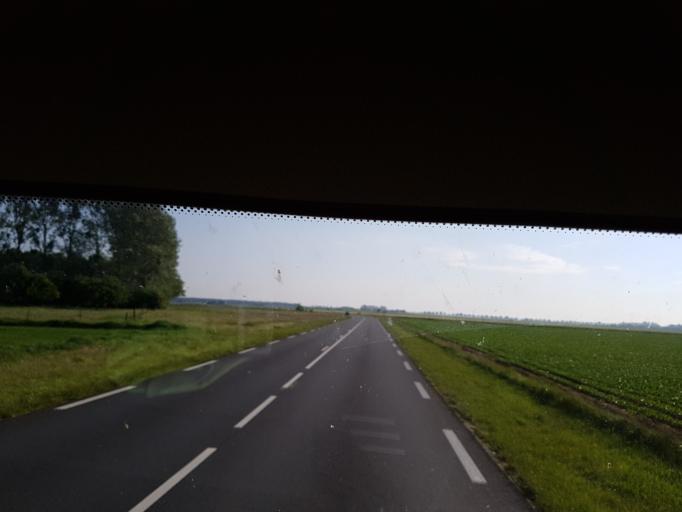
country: FR
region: Picardie
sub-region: Departement de la Somme
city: Crecy-en-Ponthieu
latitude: 50.1919
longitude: 1.8729
